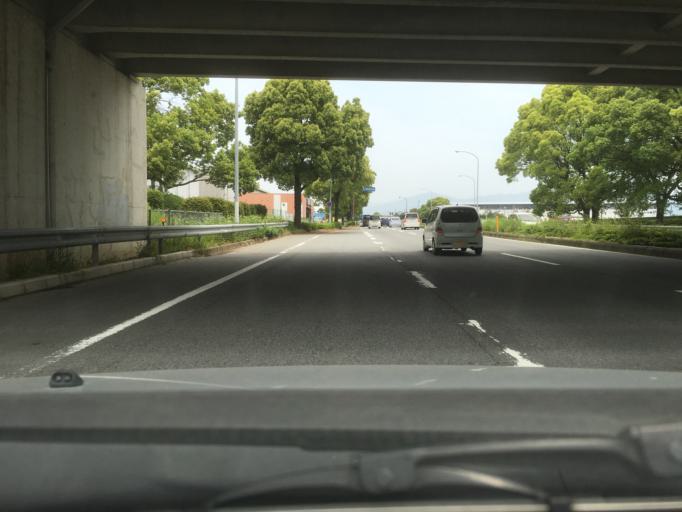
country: JP
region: Kumamoto
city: Kumamoto
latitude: 32.7930
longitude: 130.7857
